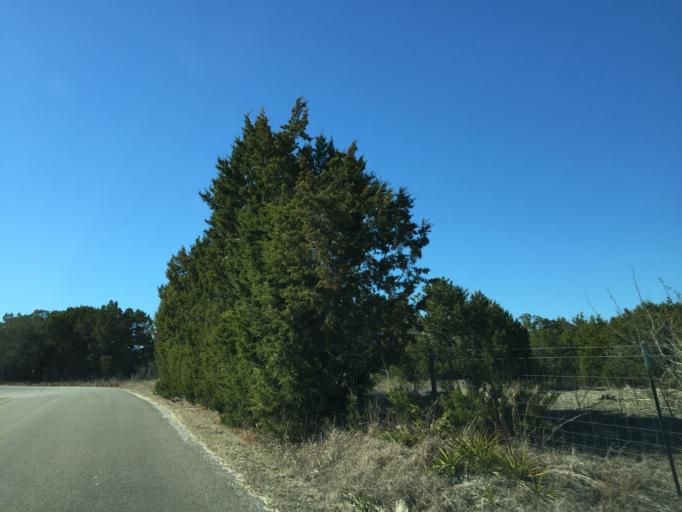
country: US
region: Texas
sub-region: Burnet County
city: Bertram
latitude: 30.8979
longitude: -98.1213
